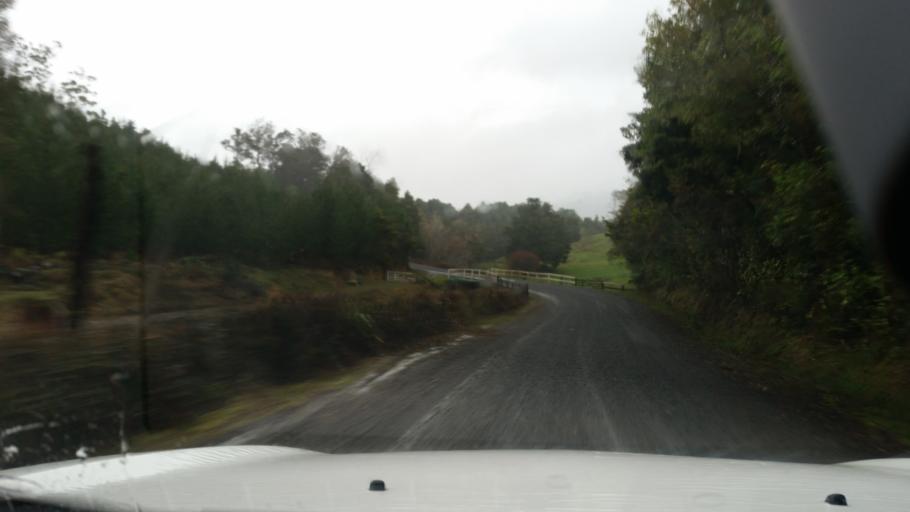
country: NZ
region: Northland
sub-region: Kaipara District
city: Dargaville
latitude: -35.7255
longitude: 173.9563
